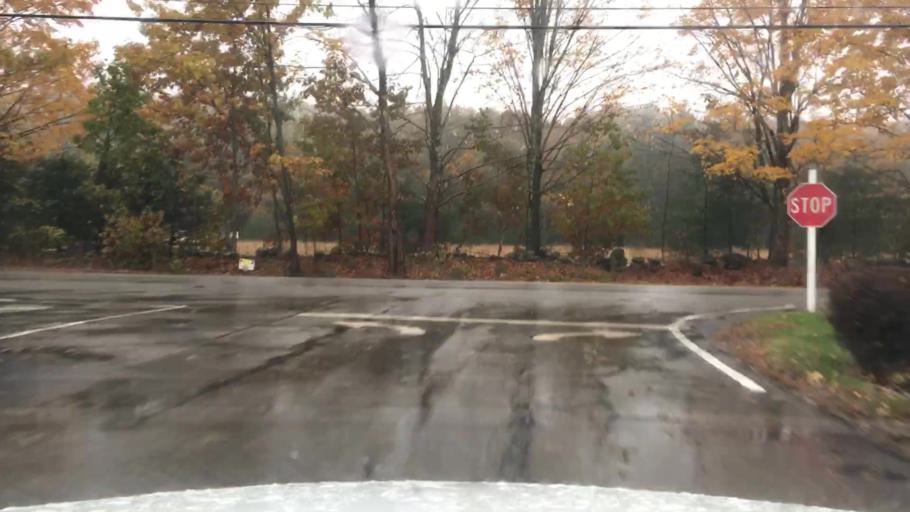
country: US
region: New Hampshire
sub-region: Strafford County
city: Rochester
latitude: 43.3131
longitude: -70.9315
